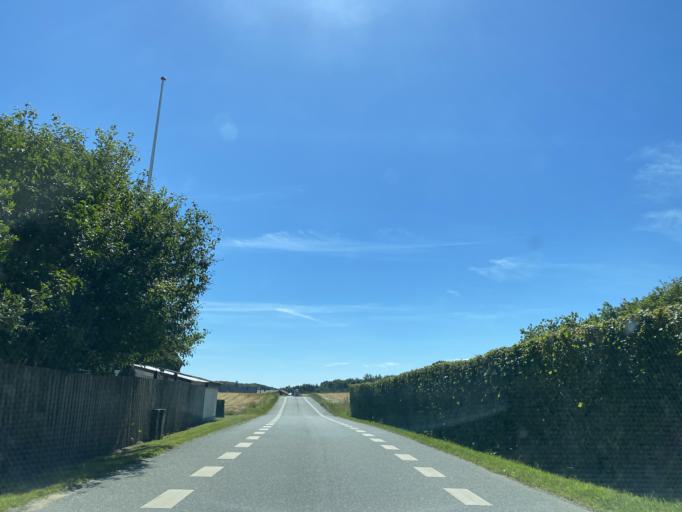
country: DK
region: South Denmark
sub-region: Vejle Kommune
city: Vejle
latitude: 55.6441
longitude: 9.5454
